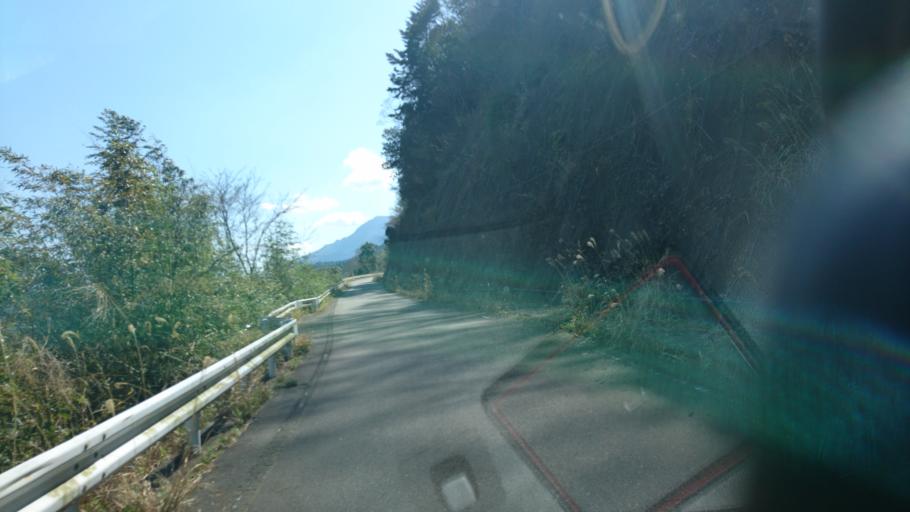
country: JP
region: Shizuoka
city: Fujinomiya
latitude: 35.3341
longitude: 138.4438
